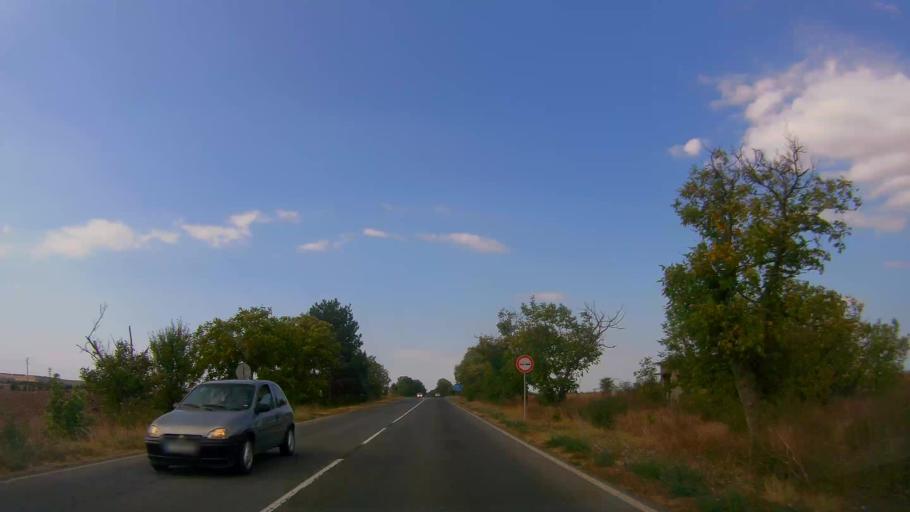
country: BG
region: Burgas
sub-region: Obshtina Aytos
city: Aytos
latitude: 42.6803
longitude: 27.1171
